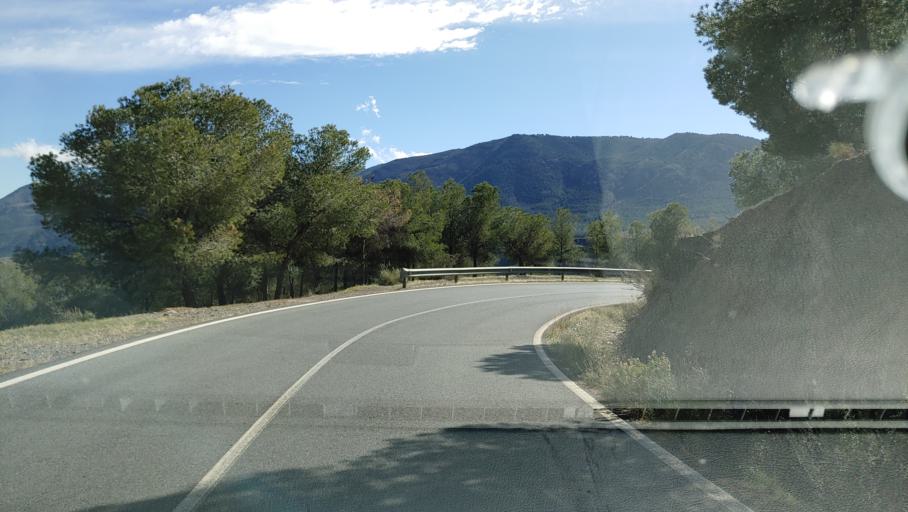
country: ES
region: Andalusia
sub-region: Provincia de Almeria
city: Canjayar
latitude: 37.0158
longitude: -2.7227
